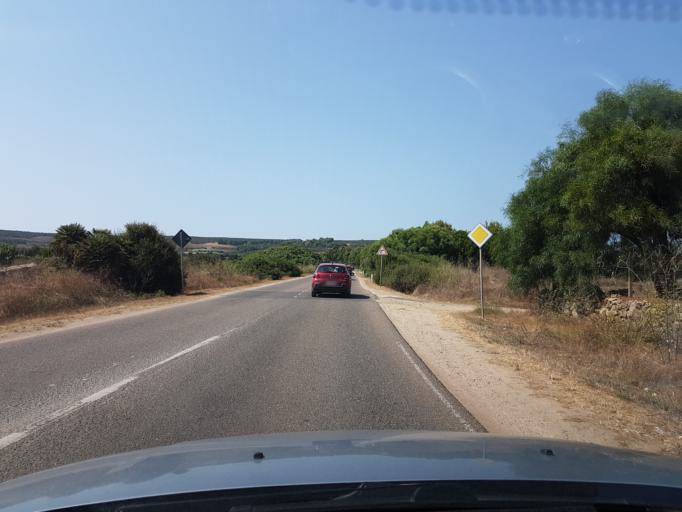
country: IT
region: Sardinia
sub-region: Provincia di Oristano
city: Cabras
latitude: 39.9161
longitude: 8.4524
